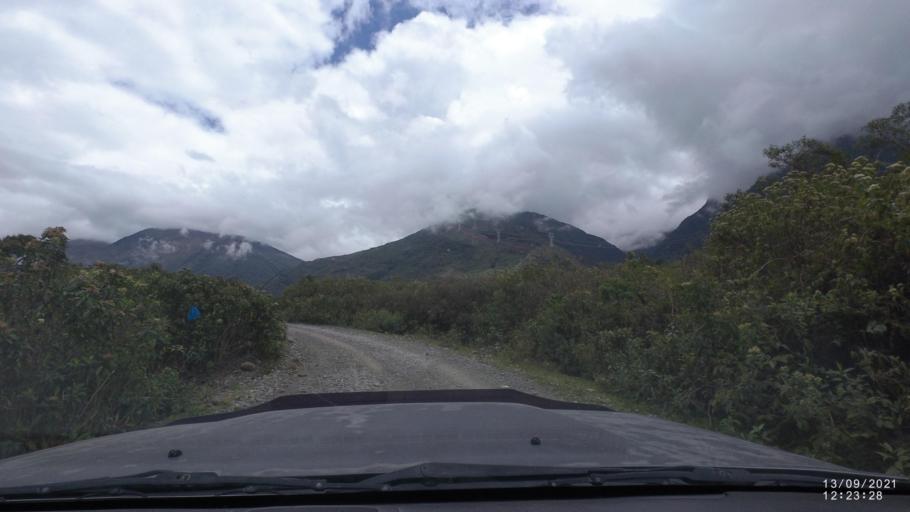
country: BO
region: Cochabamba
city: Colomi
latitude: -17.2424
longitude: -65.8182
